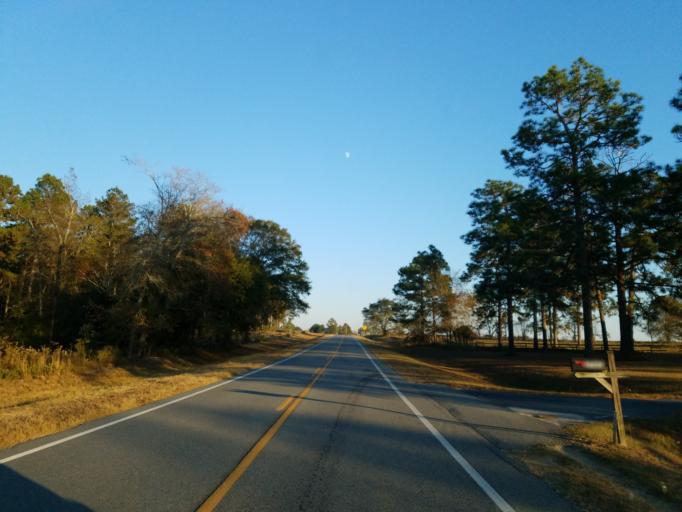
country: US
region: Georgia
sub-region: Wilcox County
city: Rochelle
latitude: 31.8169
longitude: -83.5338
